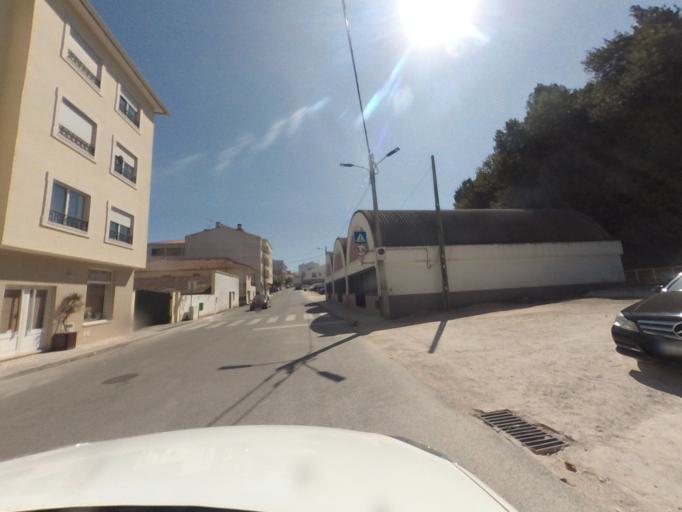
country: PT
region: Leiria
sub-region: Alcobaca
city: Turquel
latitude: 39.4656
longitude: -8.9782
